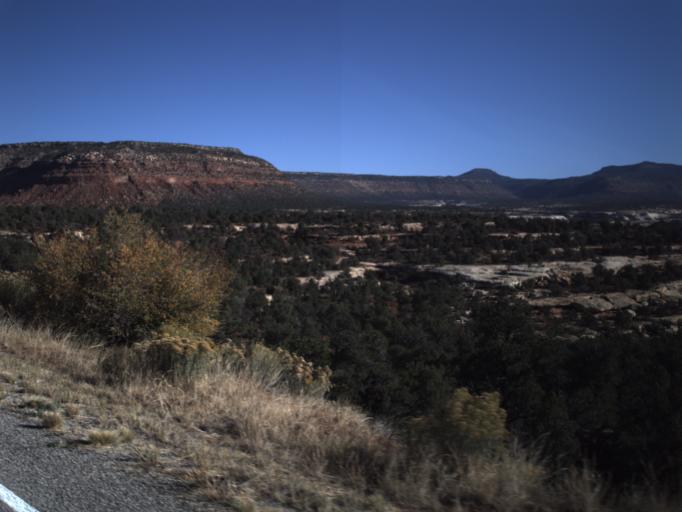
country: US
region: Utah
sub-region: San Juan County
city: Blanding
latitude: 37.5892
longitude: -110.0410
